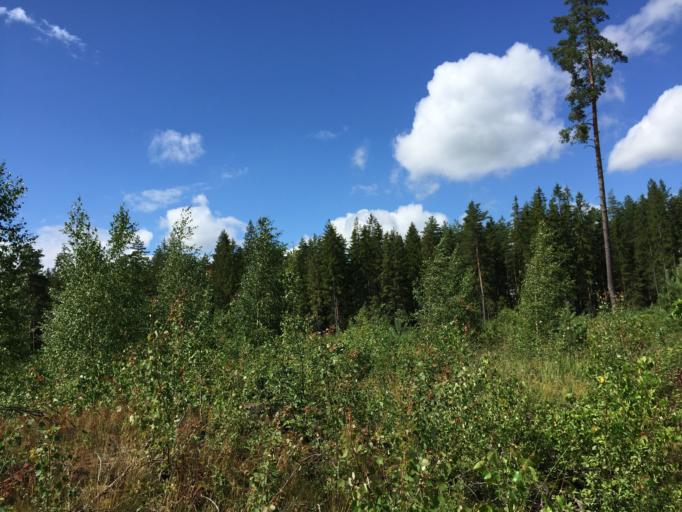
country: LV
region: Ropazu
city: Ropazi
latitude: 56.8955
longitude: 24.7181
